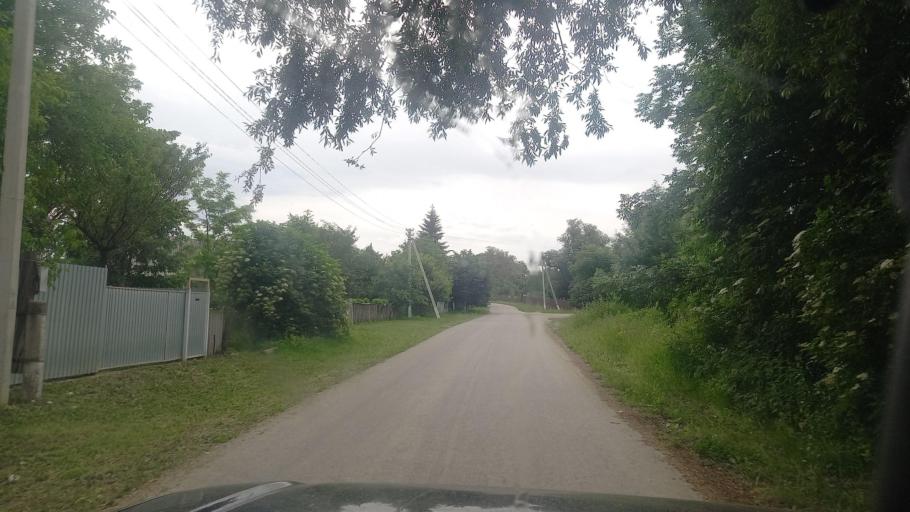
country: RU
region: Krasnodarskiy
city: Peredovaya
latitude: 44.0872
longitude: 41.3626
